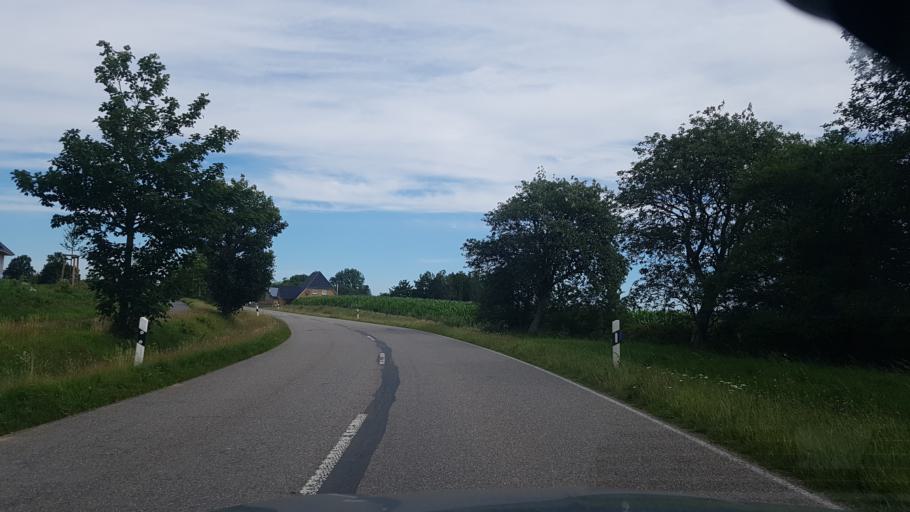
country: DE
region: Schleswig-Holstein
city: Ladelund
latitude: 54.8429
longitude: 9.0344
